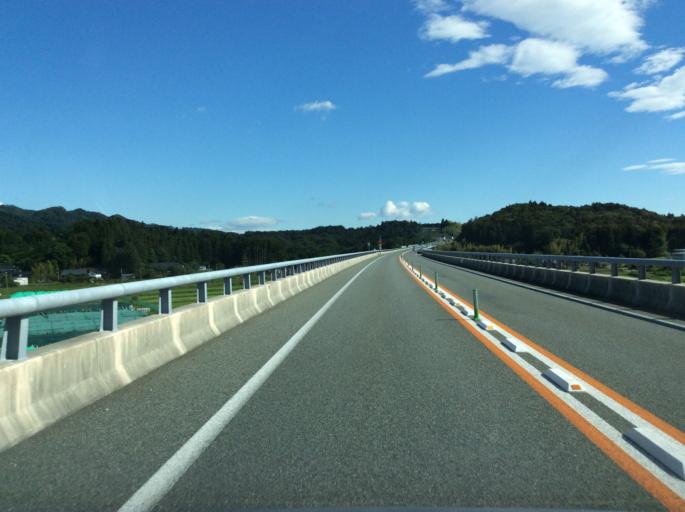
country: JP
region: Fukushima
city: Namie
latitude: 37.2787
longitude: 140.9817
